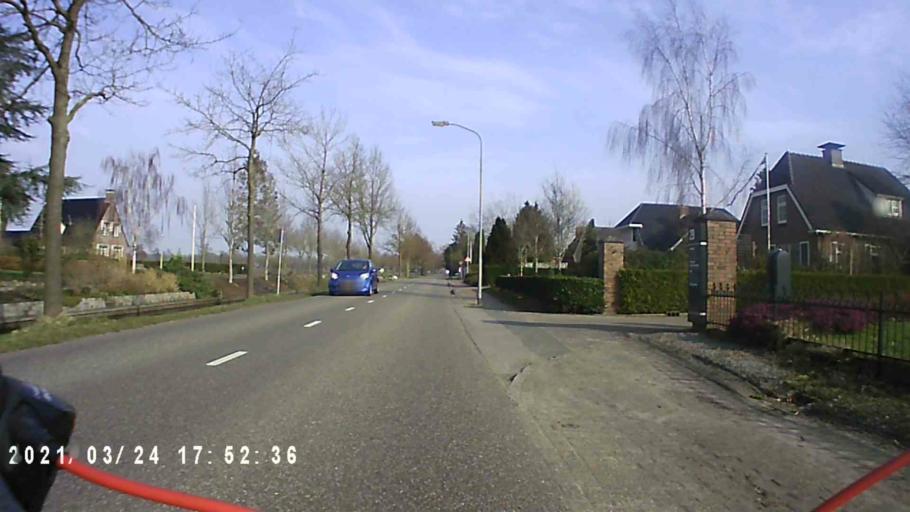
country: NL
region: Groningen
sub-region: Gemeente Leek
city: Leek
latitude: 53.1231
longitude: 6.3527
